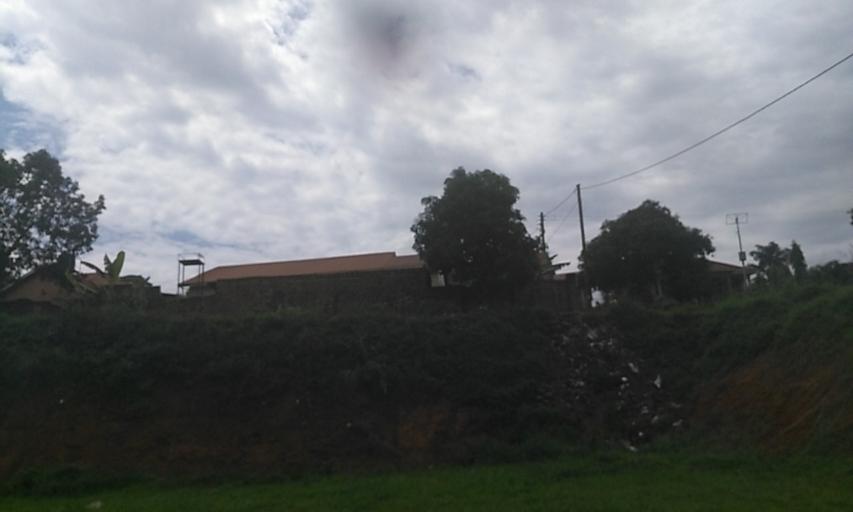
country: UG
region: Central Region
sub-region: Wakiso District
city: Kireka
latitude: 0.3615
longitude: 32.6352
